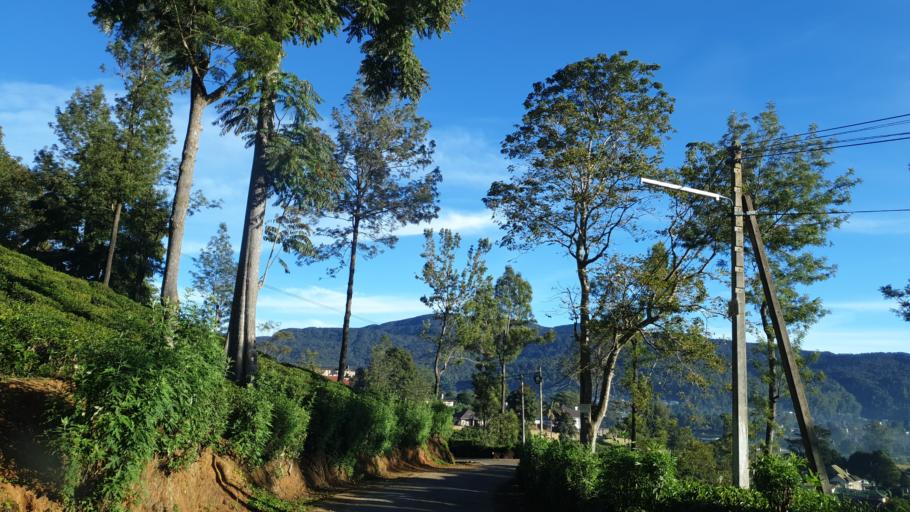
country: LK
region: Central
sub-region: Nuwara Eliya District
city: Nuwara Eliya
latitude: 6.9583
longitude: 80.7659
